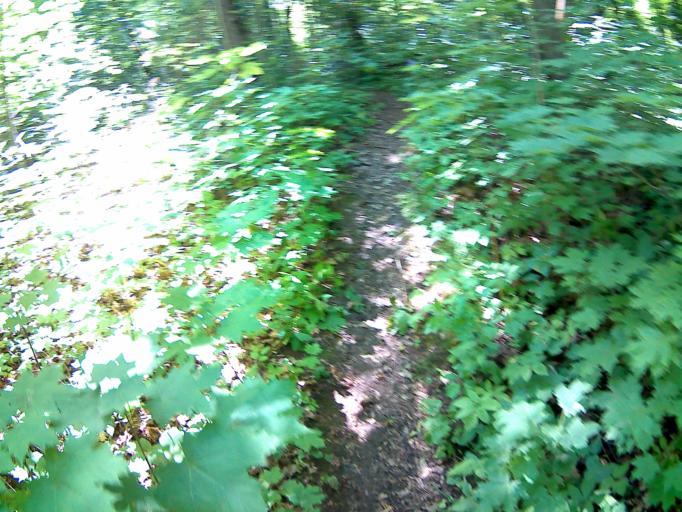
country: RU
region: Nizjnij Novgorod
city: Nizhniy Novgorod
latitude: 56.2276
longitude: 43.9228
